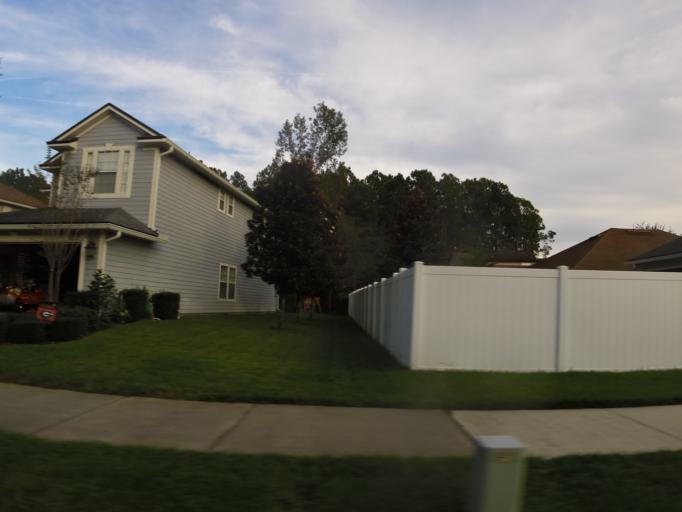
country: US
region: Florida
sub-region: Saint Johns County
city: Fruit Cove
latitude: 30.1503
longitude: -81.5416
